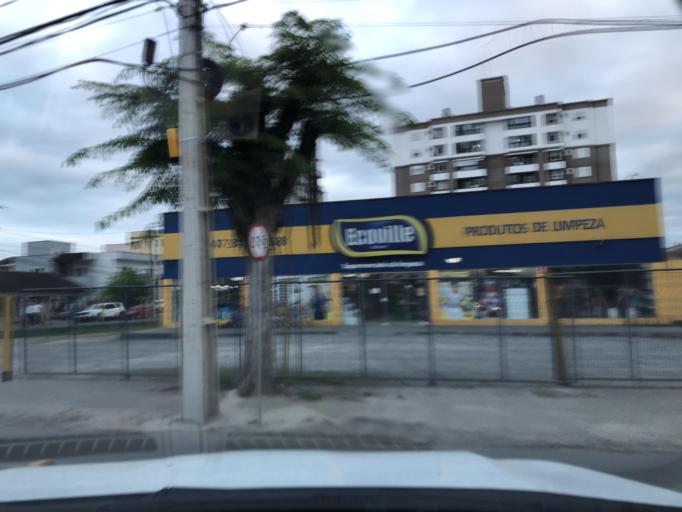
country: BR
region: Santa Catarina
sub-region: Joinville
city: Joinville
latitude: -26.2737
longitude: -48.8715
